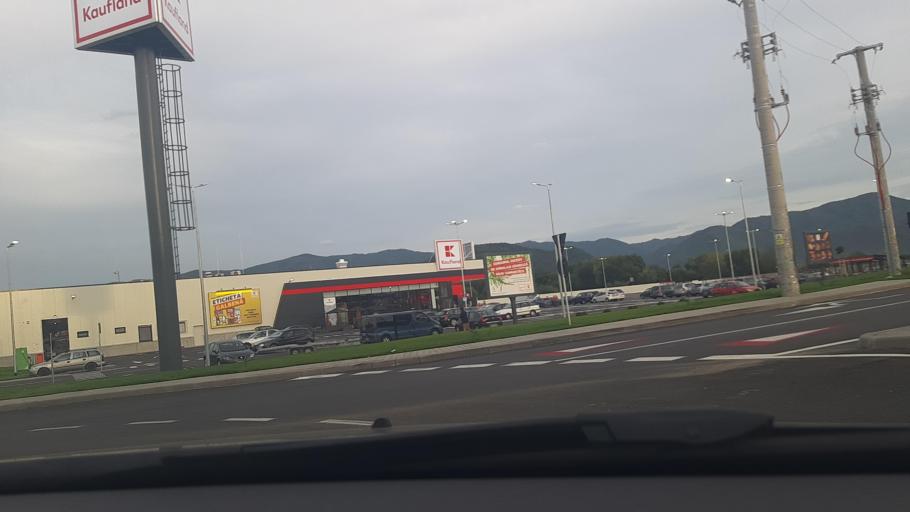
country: RO
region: Hunedoara
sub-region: Oras Hateg
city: Hateg
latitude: 45.6076
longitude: 22.9570
